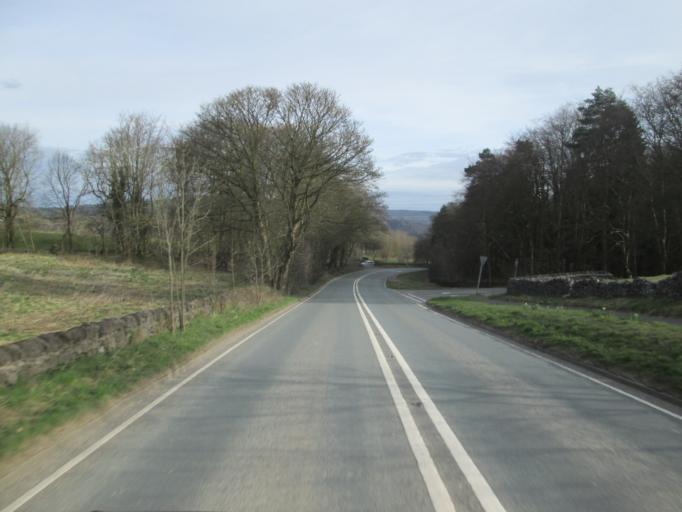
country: GB
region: England
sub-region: Derbyshire
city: Cromford
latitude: 53.0980
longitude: -1.5692
